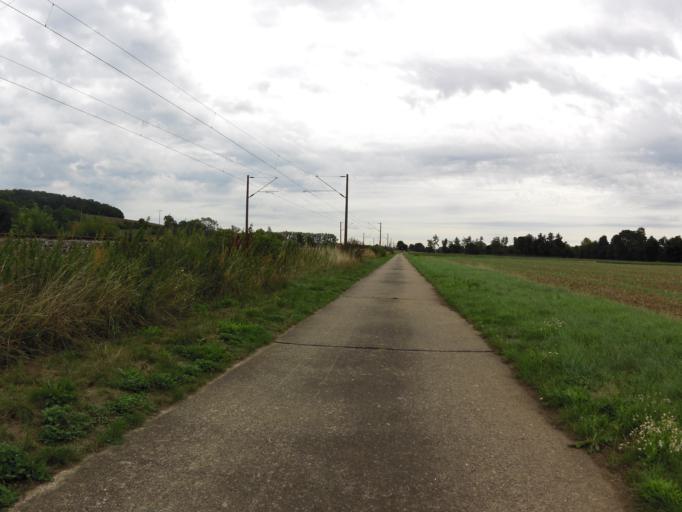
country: DE
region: Bavaria
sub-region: Regierungsbezirk Unterfranken
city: Gadheim
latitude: 50.0173
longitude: 10.3909
